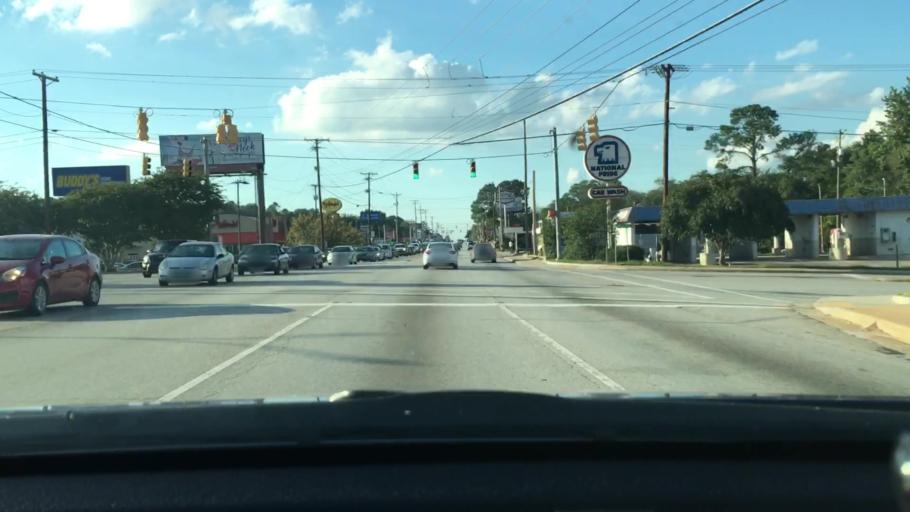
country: US
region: South Carolina
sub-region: Lexington County
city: Saint Andrews
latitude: 34.0417
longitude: -81.0968
